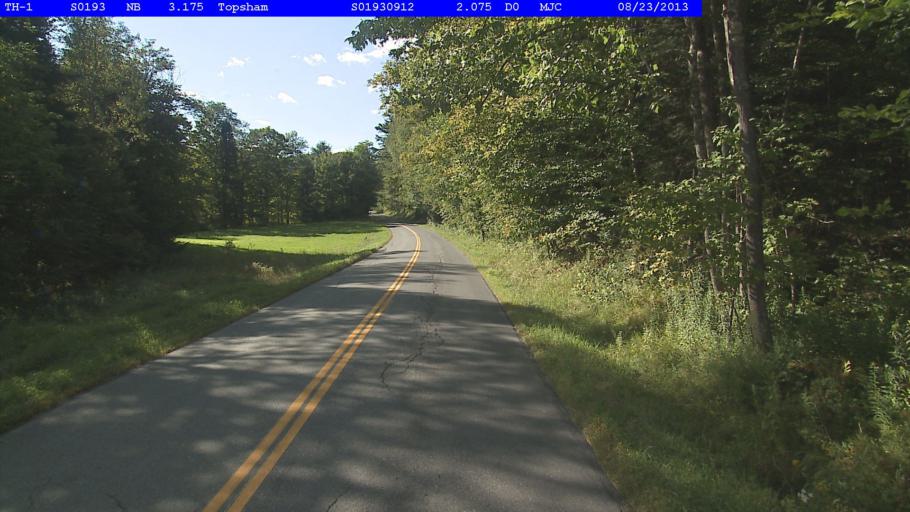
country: US
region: New Hampshire
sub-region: Grafton County
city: Haverhill
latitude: 44.0996
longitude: -72.2250
